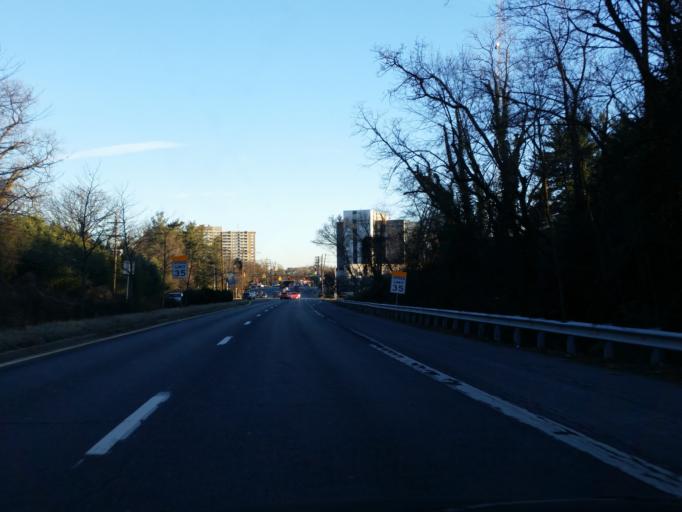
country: US
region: Maryland
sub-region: Montgomery County
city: Somerset
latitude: 38.9676
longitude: -77.1079
